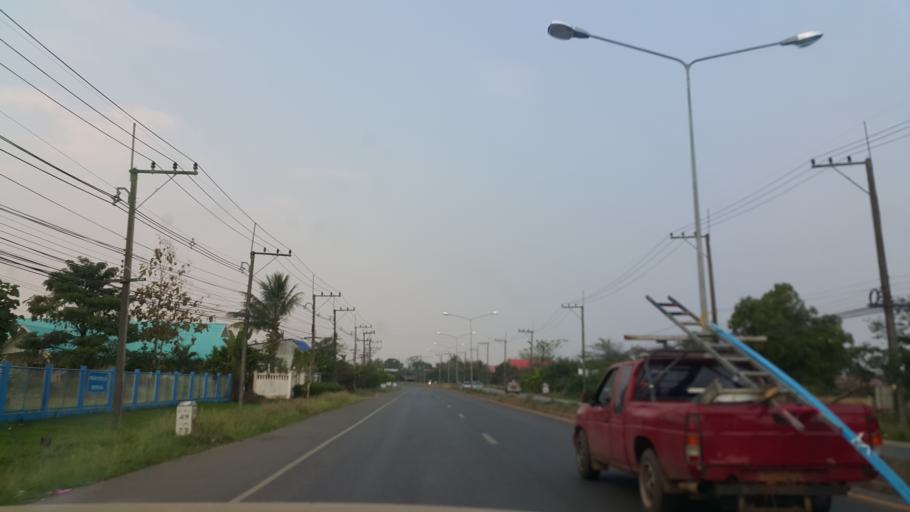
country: TH
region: Nakhon Phanom
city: That Phanom
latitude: 16.9816
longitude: 104.7278
